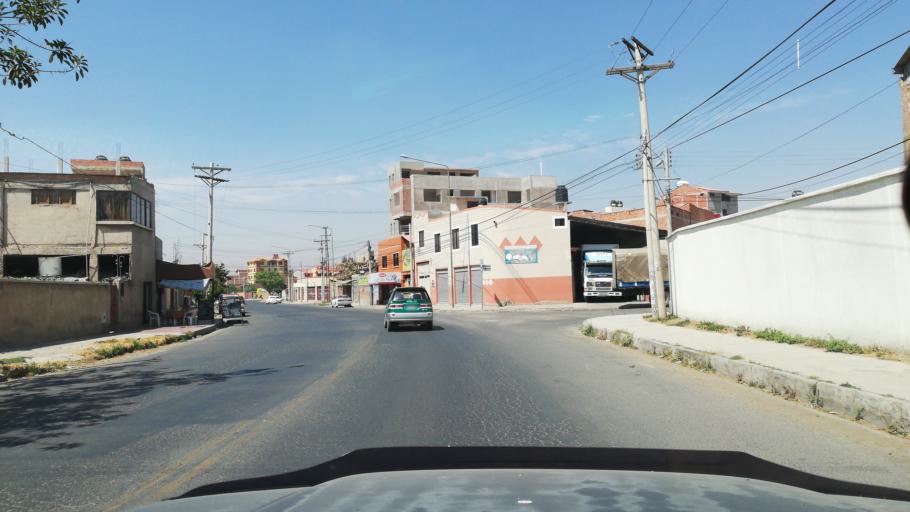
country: BO
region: Cochabamba
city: Cochabamba
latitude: -17.4163
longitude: -66.1688
